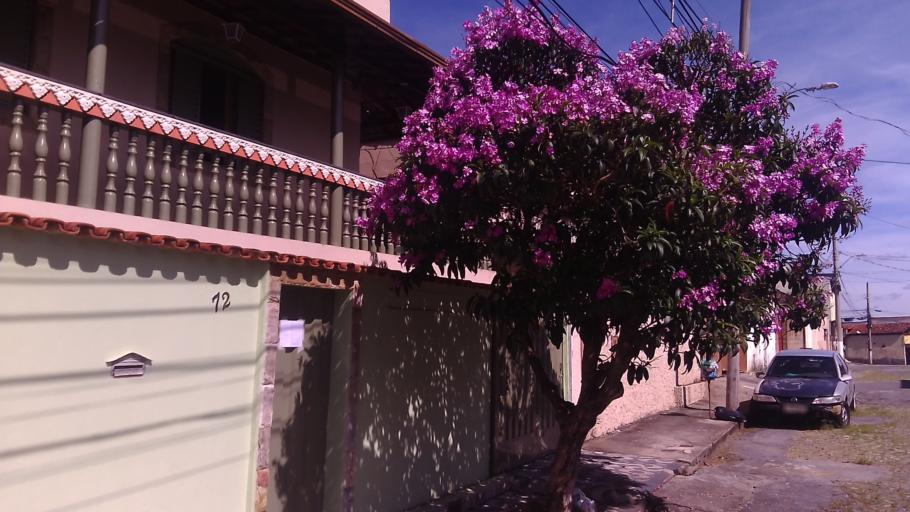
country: BR
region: Minas Gerais
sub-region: Contagem
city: Contagem
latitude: -19.9106
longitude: -44.0055
